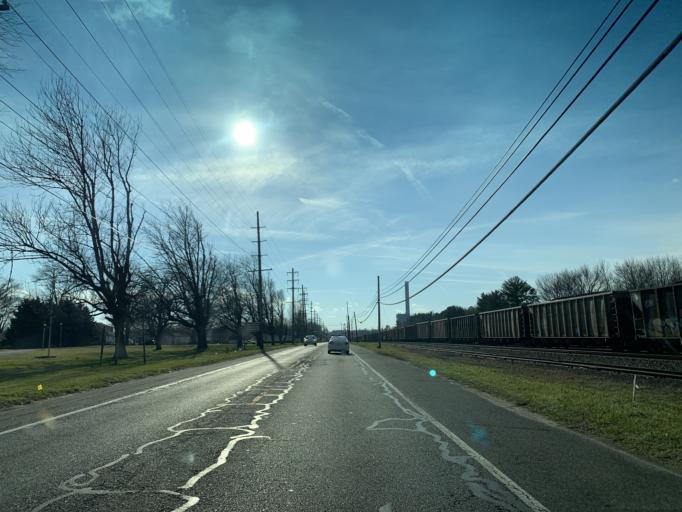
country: US
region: New Jersey
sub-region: Salem County
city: Carneys Point
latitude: 39.7016
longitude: -75.4751
